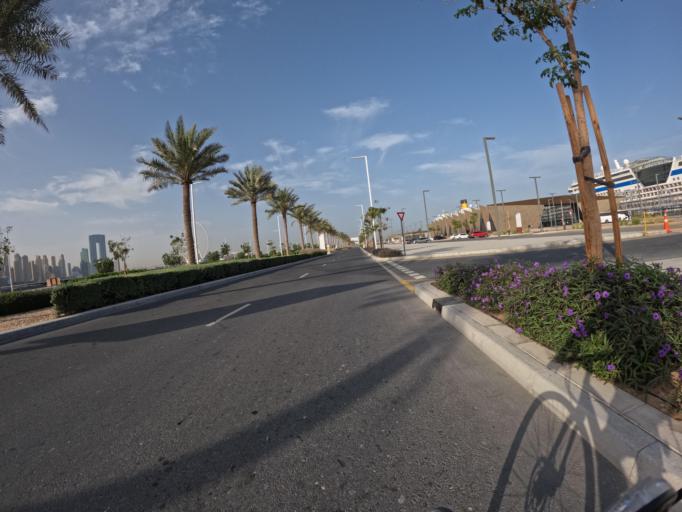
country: AE
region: Dubai
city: Dubai
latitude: 25.0940
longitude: 55.1342
